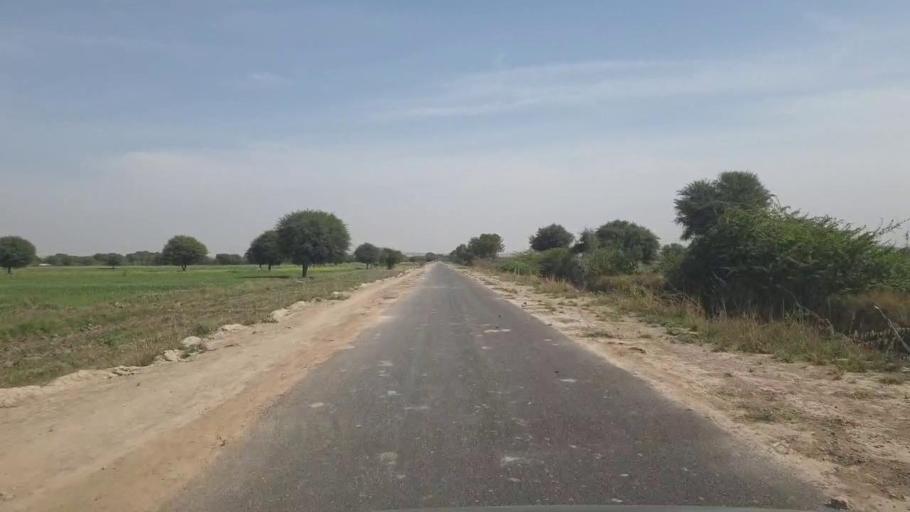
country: PK
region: Sindh
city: Kunri
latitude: 25.1881
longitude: 69.6804
